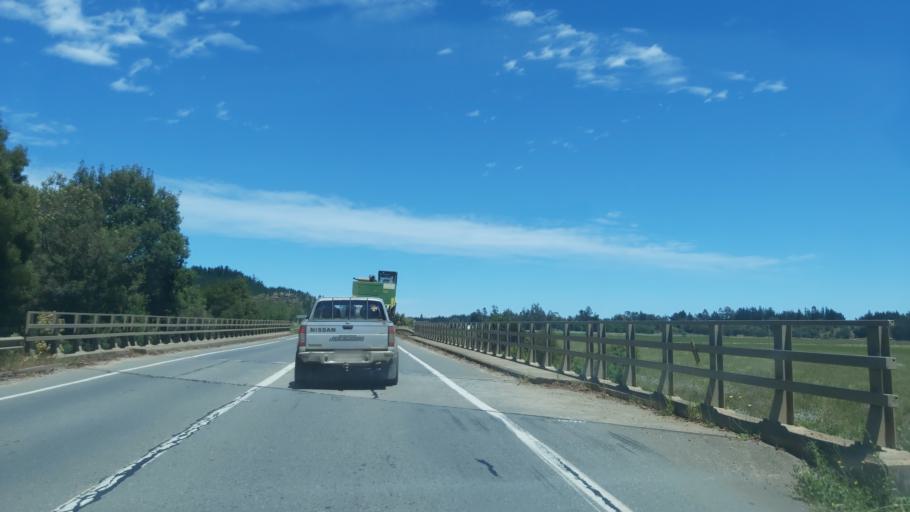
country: CL
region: Maule
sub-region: Provincia de Talca
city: Constitucion
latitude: -35.2767
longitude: -72.3495
